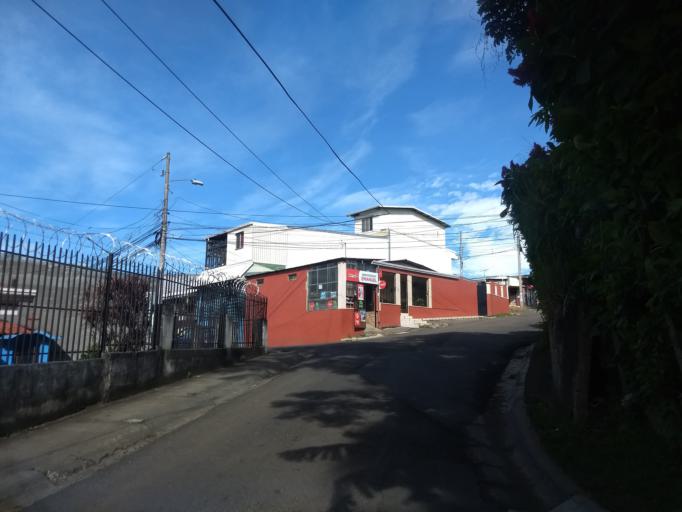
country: CR
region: Heredia
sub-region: Canton de Belen
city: San Antonio
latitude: 9.9764
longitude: -84.1972
